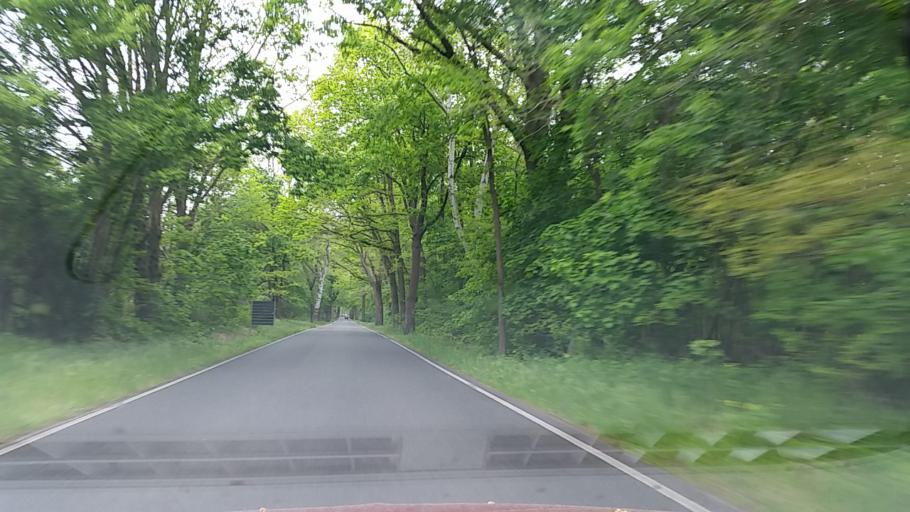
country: DE
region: Brandenburg
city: Diensdorf-Radlow
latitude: 52.2574
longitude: 14.0399
